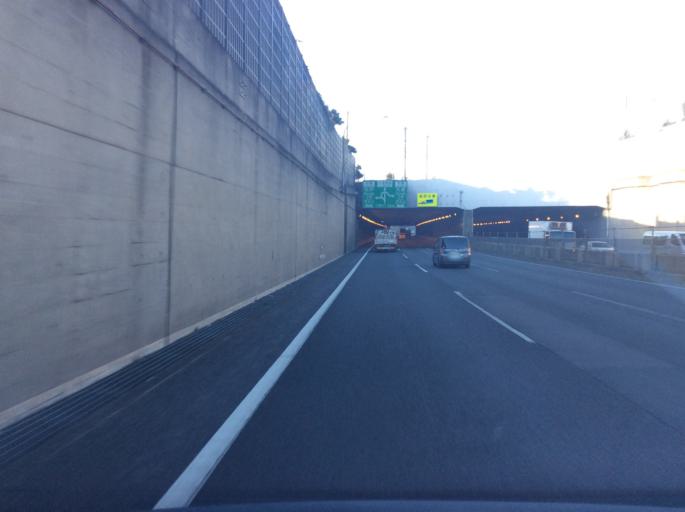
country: JP
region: Chiba
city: Nagareyama
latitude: 35.8533
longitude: 139.8773
